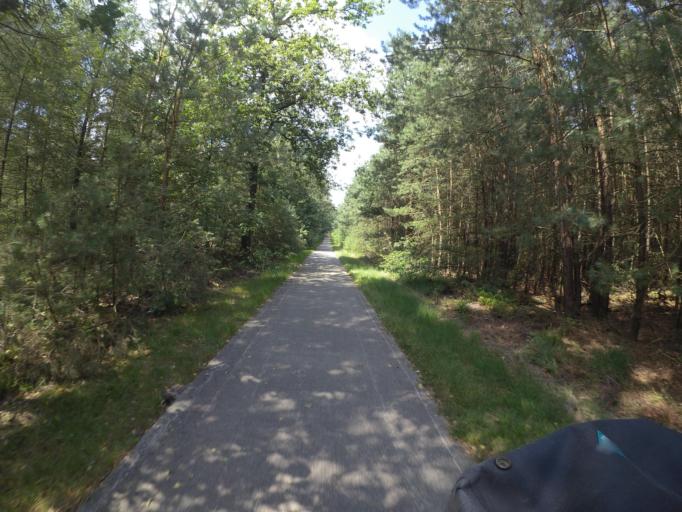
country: NL
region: Gelderland
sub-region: Gemeente Heerde
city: Heerde
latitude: 52.4180
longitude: 6.0250
